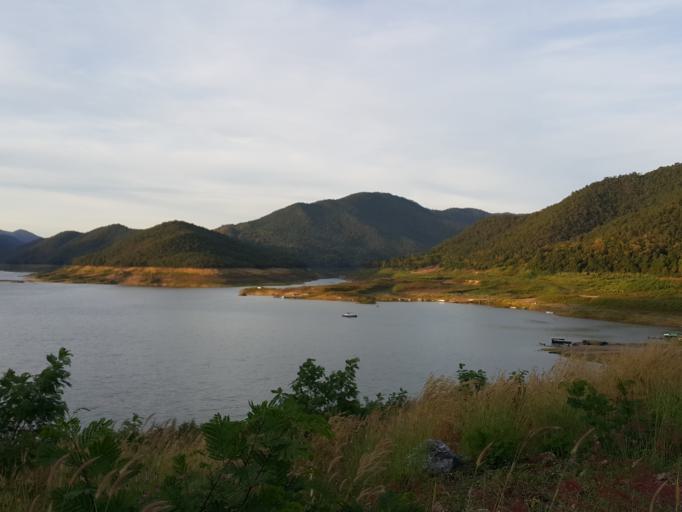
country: TH
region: Chiang Mai
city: San Sai
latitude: 18.9370
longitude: 99.1369
